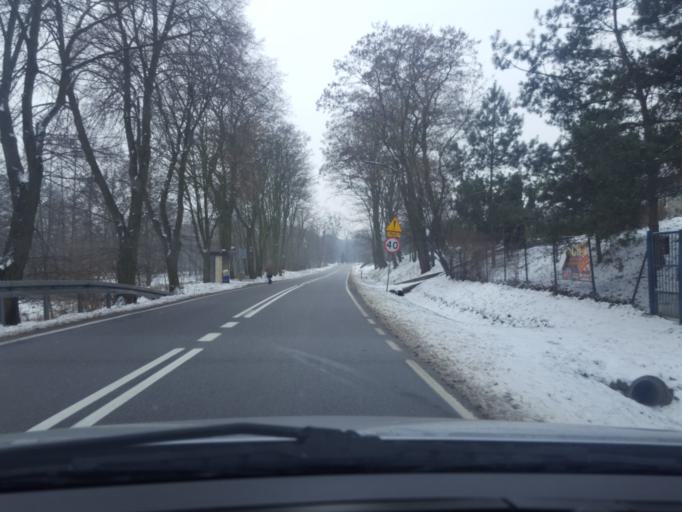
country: PL
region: Lodz Voivodeship
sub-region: Powiat brzezinski
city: Rogow
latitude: 51.8673
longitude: 19.8377
